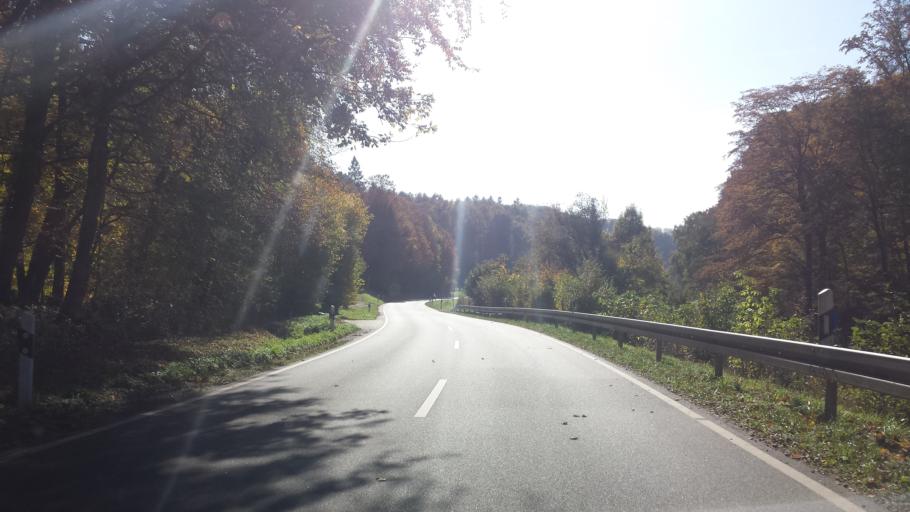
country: DE
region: Hesse
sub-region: Regierungsbezirk Darmstadt
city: Seeheim-Jugenheim
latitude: 49.7242
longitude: 8.6581
